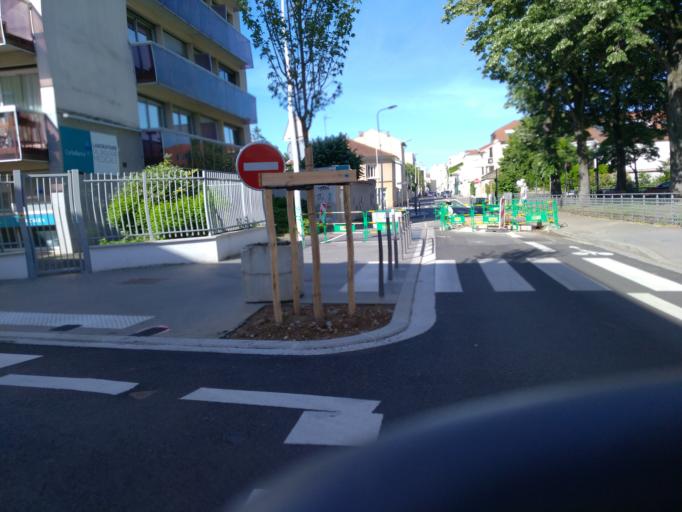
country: FR
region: Rhone-Alpes
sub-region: Departement du Rhone
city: Villeurbanne
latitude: 45.7492
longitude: 4.8877
